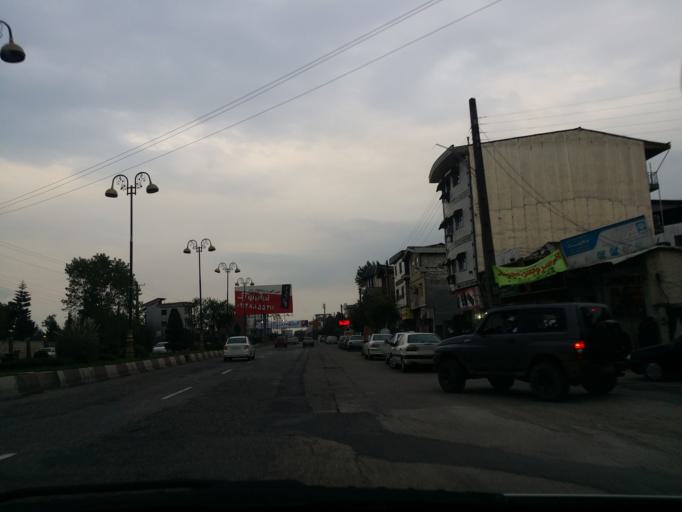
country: IR
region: Mazandaran
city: `Abbasabad
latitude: 36.7259
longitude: 51.1181
